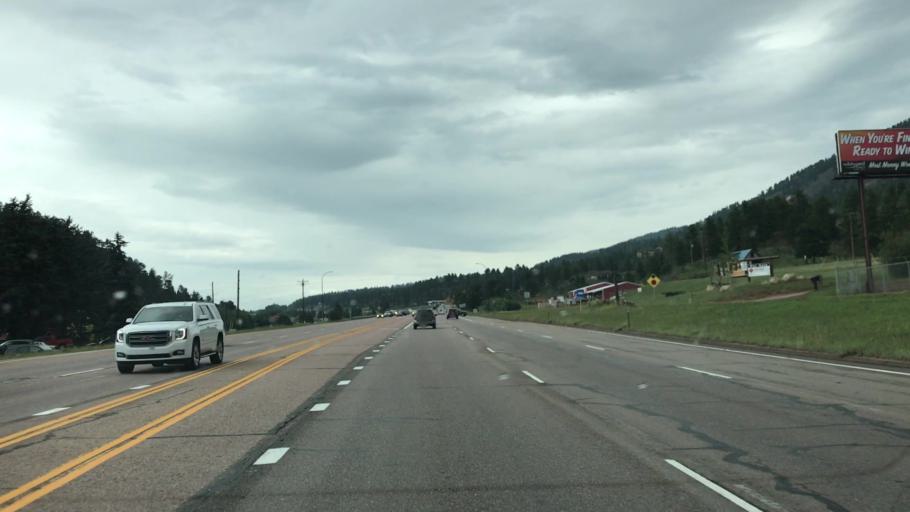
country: US
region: Colorado
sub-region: El Paso County
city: Cascade-Chipita Park
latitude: 38.9555
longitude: -105.0272
